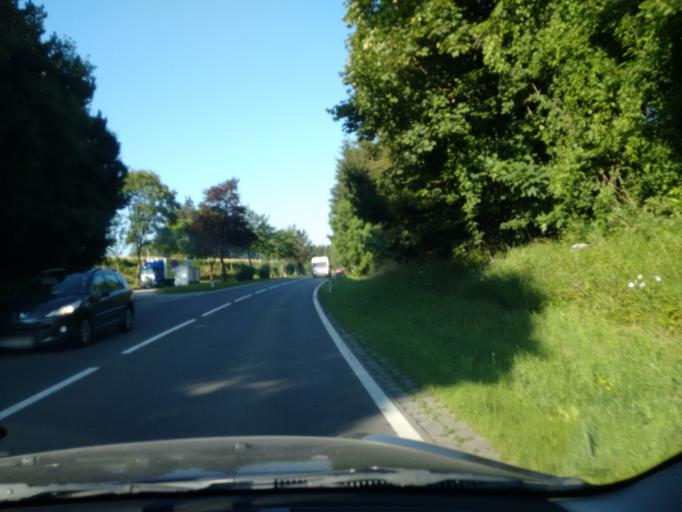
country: AT
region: Upper Austria
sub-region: Politischer Bezirk Gmunden
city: Gmunden
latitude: 47.9218
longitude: 13.7819
